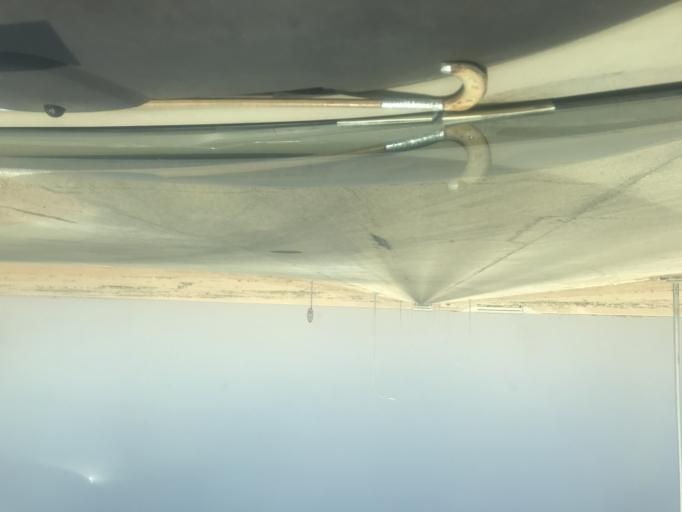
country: SA
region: Ar Riyad
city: Riyadh
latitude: 24.9913
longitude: 46.6962
